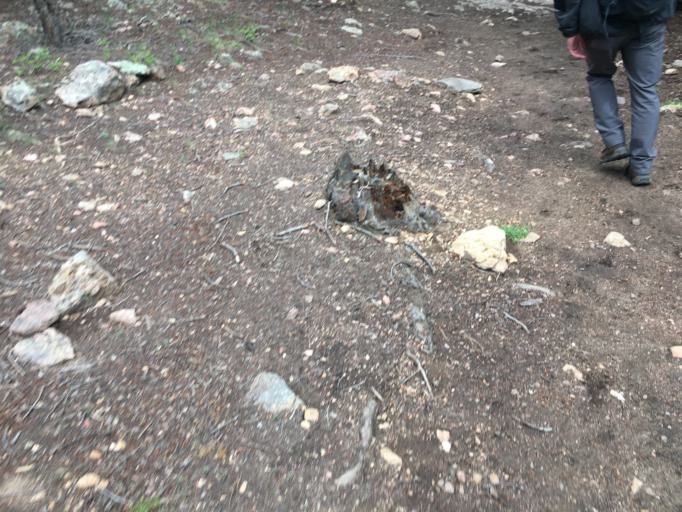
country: US
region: Colorado
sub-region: Larimer County
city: Estes Park
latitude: 40.3428
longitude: -105.5876
